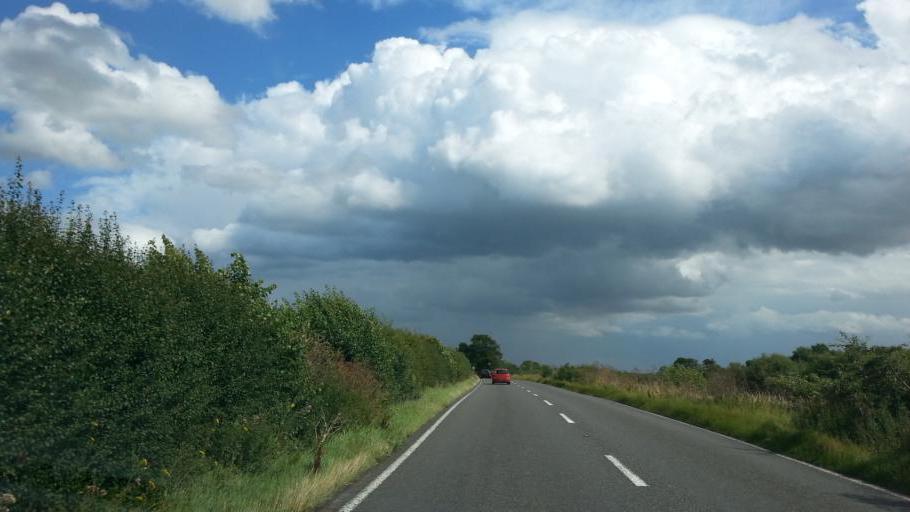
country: GB
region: England
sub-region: Nottinghamshire
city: Southwell
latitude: 53.1076
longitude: -0.9580
